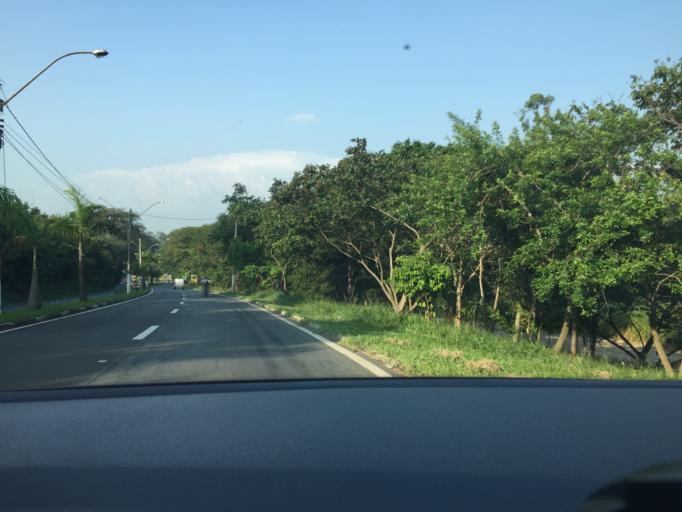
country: BR
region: Sao Paulo
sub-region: Valinhos
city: Valinhos
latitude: -23.0039
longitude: -47.0112
